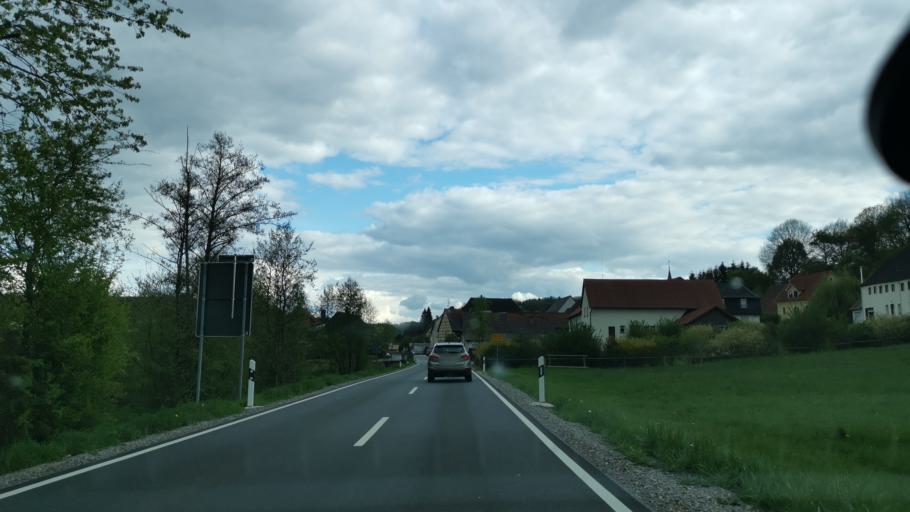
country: DE
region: Baden-Wuerttemberg
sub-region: Karlsruhe Region
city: Osterburken
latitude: 49.4750
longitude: 9.4088
